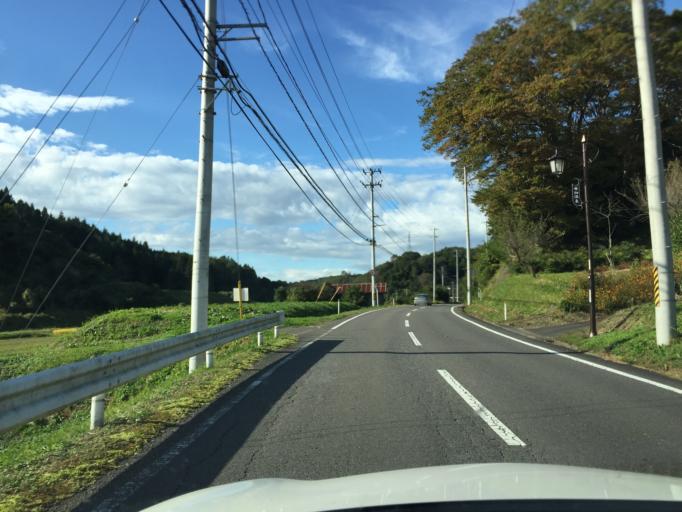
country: JP
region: Fukushima
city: Ishikawa
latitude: 37.1799
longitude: 140.4638
